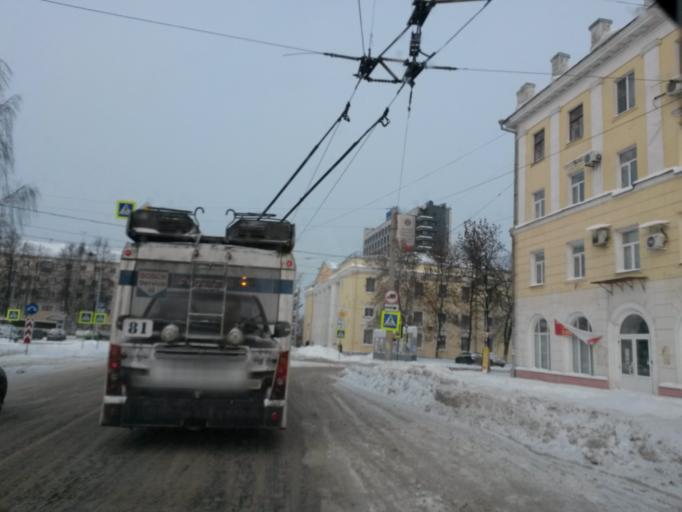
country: RU
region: Jaroslavl
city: Yaroslavl
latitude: 57.6264
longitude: 39.8371
